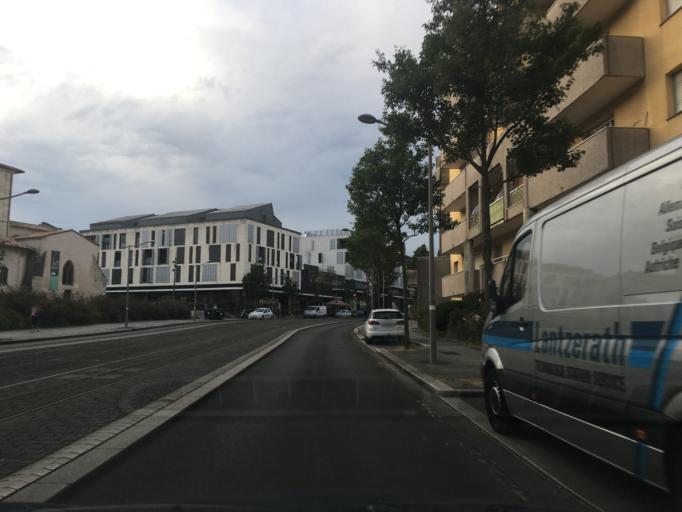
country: FR
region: Aquitaine
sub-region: Departement de la Gironde
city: Merignac
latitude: 44.8400
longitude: -0.6469
